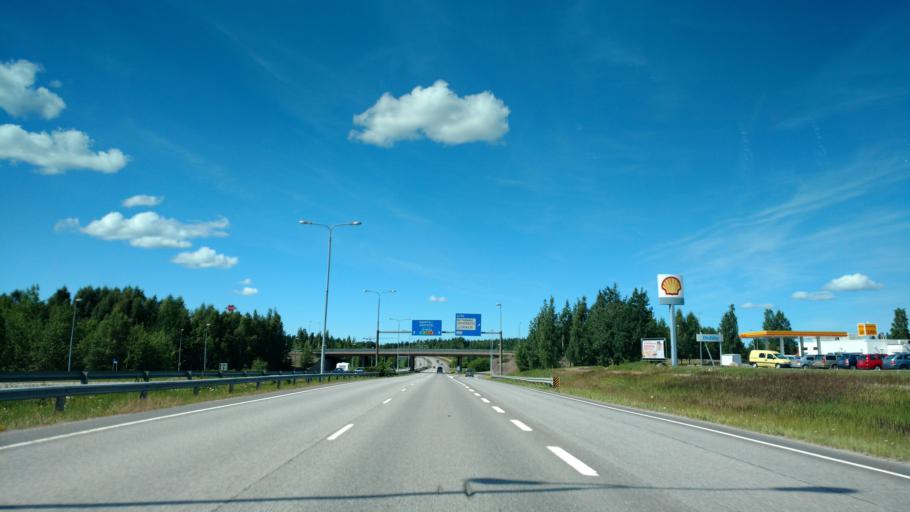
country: FI
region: Varsinais-Suomi
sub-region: Turku
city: Turku
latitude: 60.4850
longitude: 22.3228
